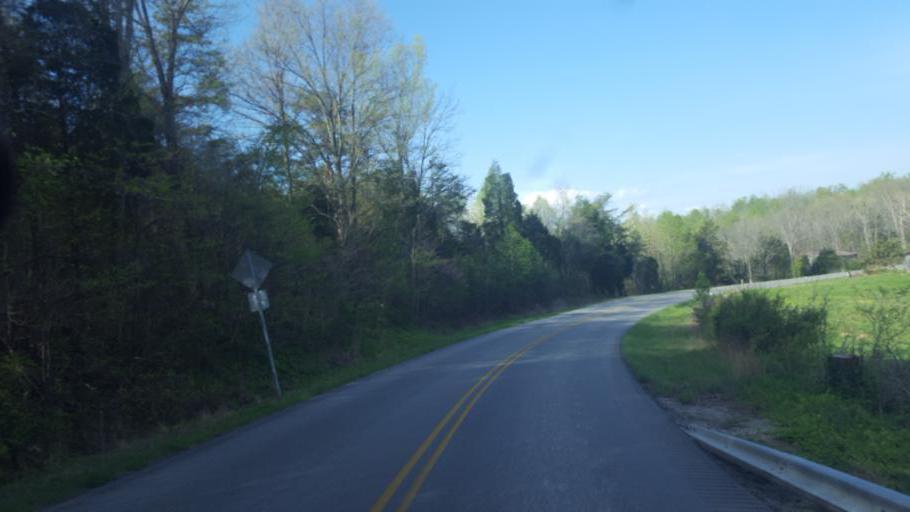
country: US
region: Kentucky
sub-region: Hart County
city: Munfordville
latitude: 37.3169
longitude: -86.0861
